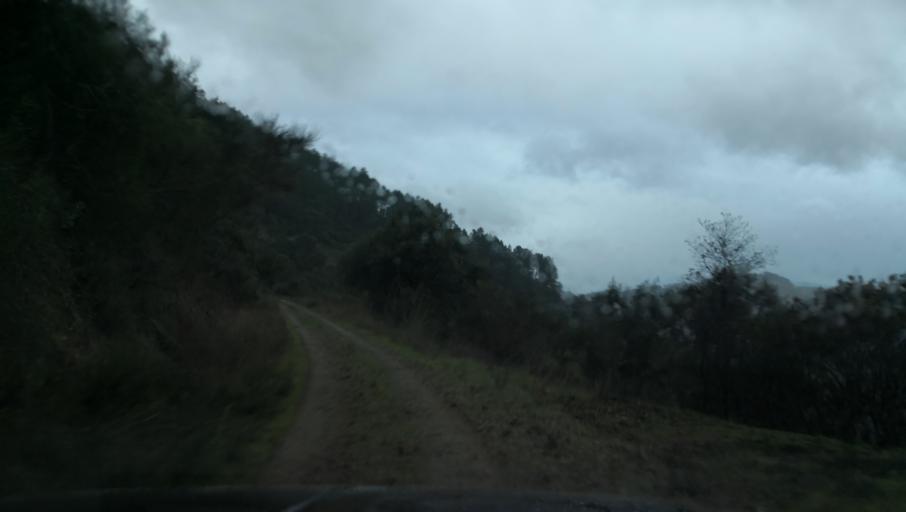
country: PT
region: Vila Real
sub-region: Vila Real
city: Vila Real
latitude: 41.2659
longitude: -7.7437
